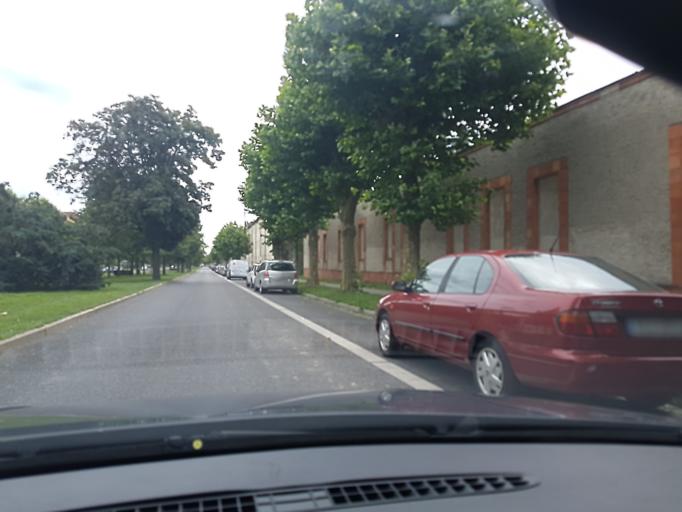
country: DE
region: Brandenburg
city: Velten
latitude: 52.6860
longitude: 13.1730
